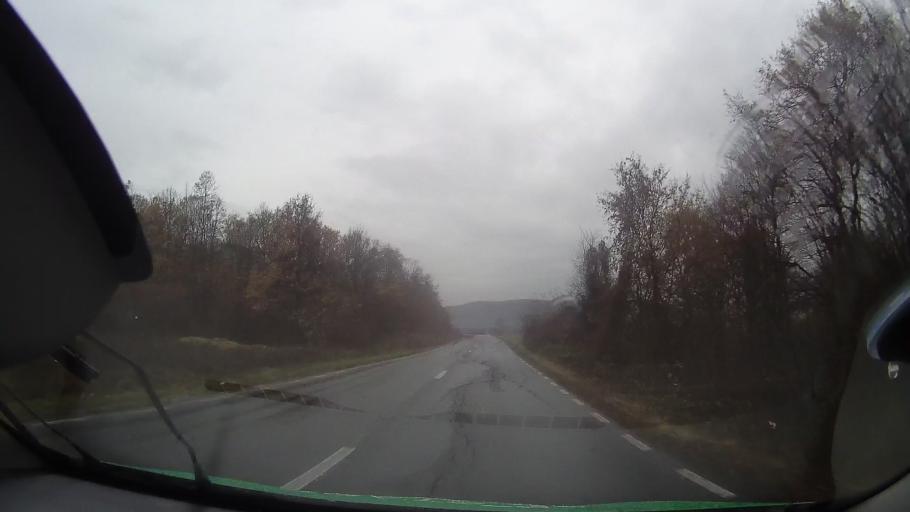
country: RO
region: Bihor
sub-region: Comuna Rabagani
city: Rabagani
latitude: 46.7358
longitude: 22.2306
